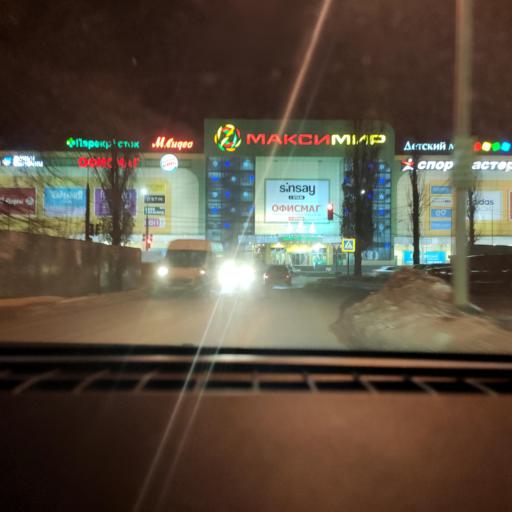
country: RU
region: Voronezj
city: Voronezh
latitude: 51.6978
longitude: 39.2711
